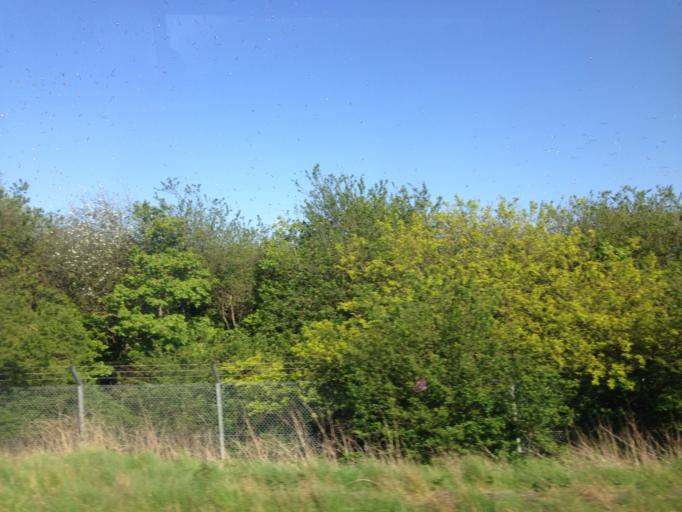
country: GB
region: England
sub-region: Greater London
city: Carshalton
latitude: 51.3830
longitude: -0.1531
